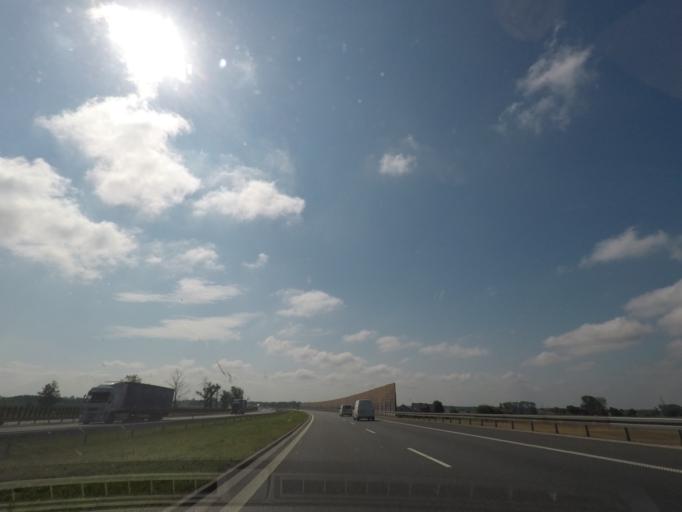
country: PL
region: Kujawsko-Pomorskie
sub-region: Powiat aleksandrowski
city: Raciazek
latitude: 52.8230
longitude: 18.8038
